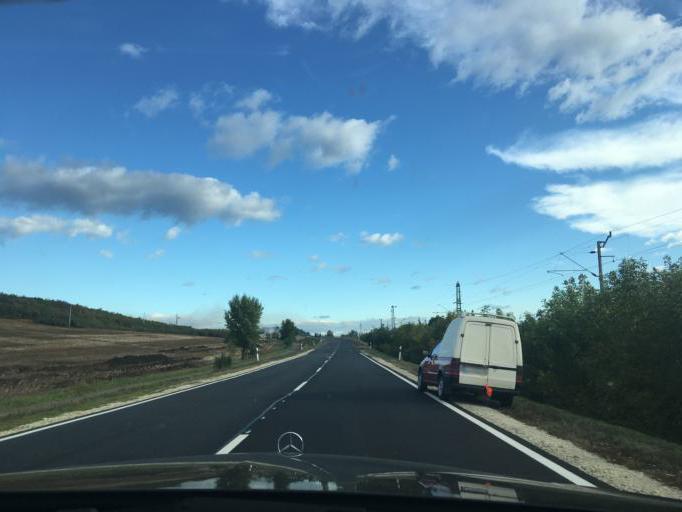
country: HU
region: Borsod-Abauj-Zemplen
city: Encs
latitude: 48.3945
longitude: 21.1618
